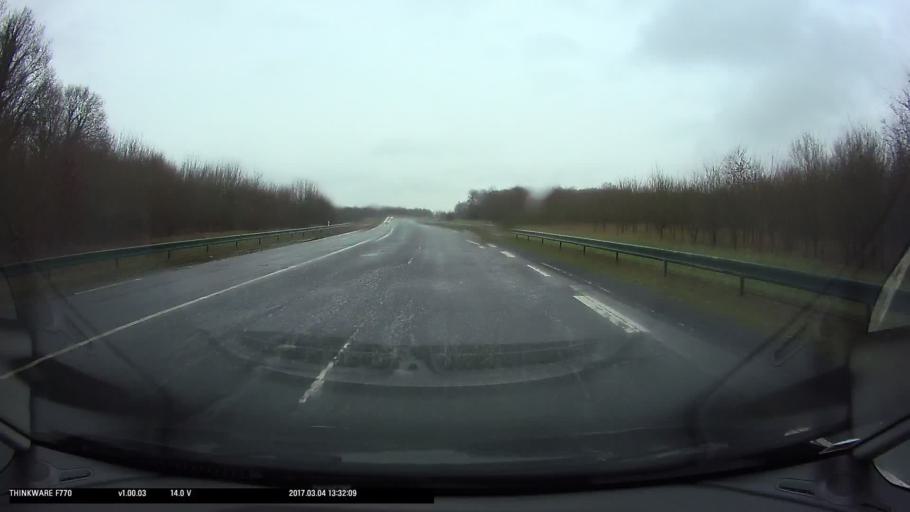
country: FR
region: Ile-de-France
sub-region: Departement du Val-d'Oise
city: Marines
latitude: 49.1320
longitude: 1.9849
